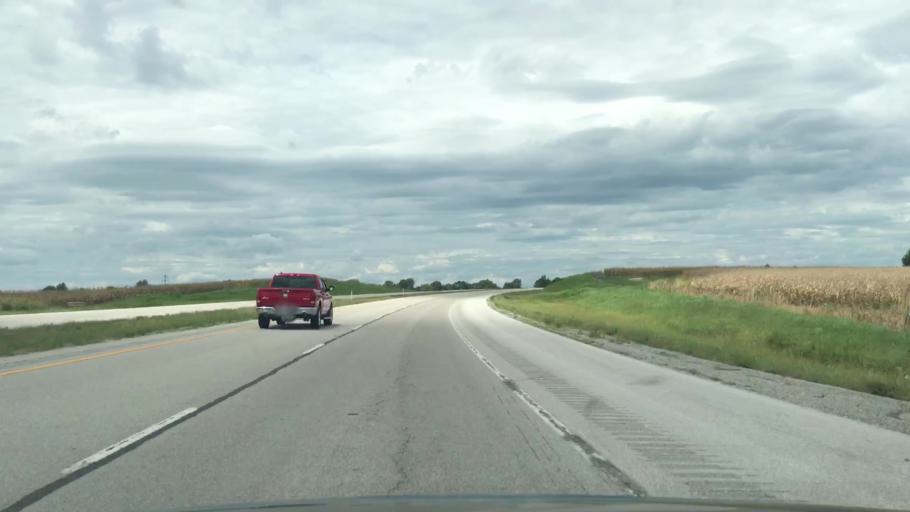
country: US
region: Kentucky
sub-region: Todd County
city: Elkton
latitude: 36.8110
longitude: -87.1363
